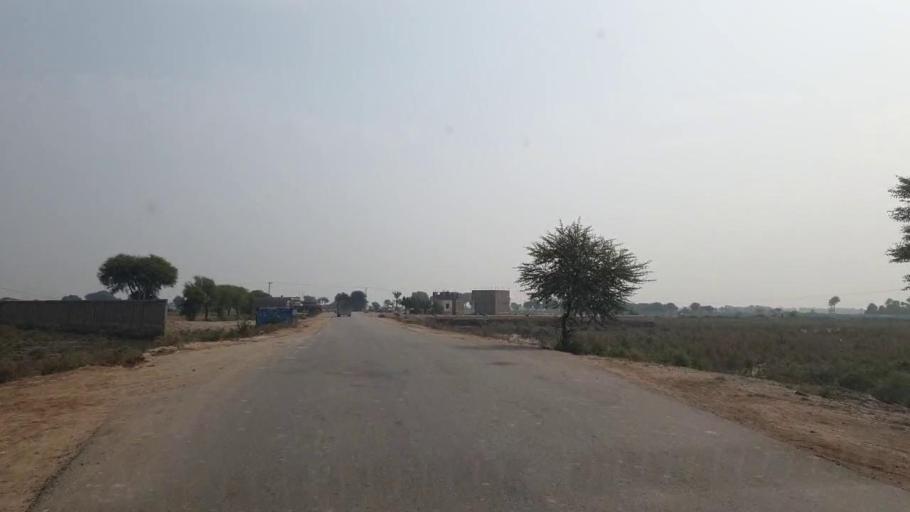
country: PK
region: Sindh
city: Matli
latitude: 25.0536
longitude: 68.6782
